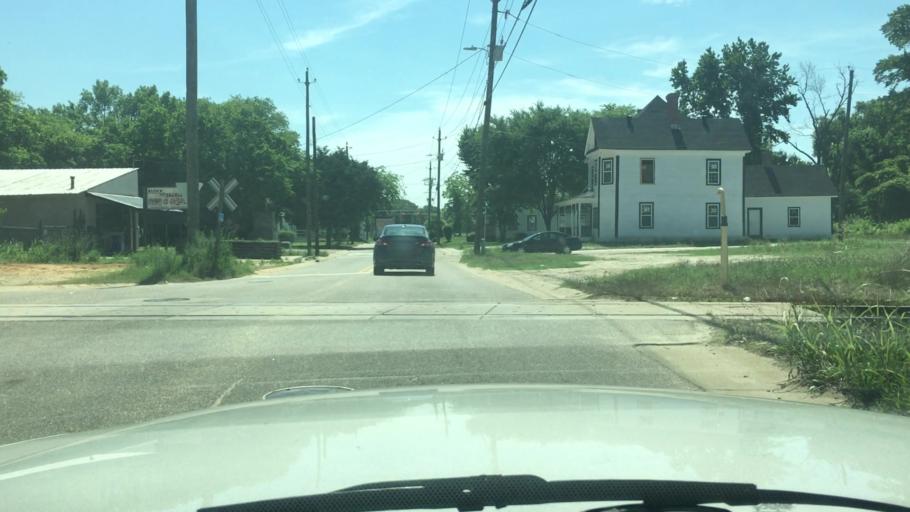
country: US
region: North Carolina
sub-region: Cumberland County
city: Fayetteville
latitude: 35.0468
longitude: -78.8828
